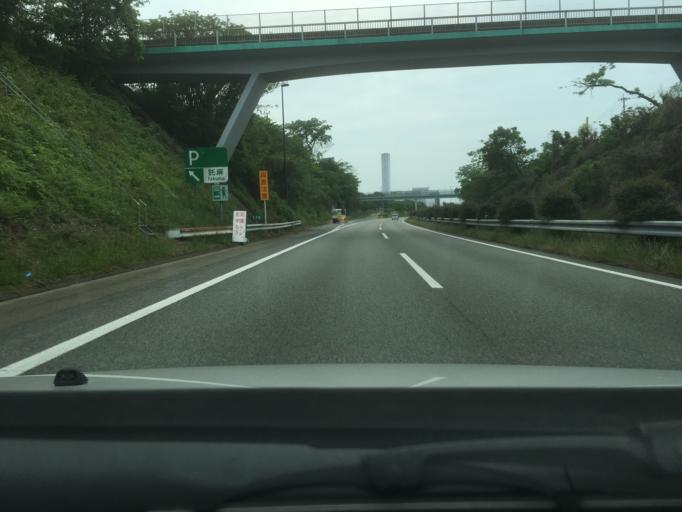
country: JP
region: Kumamoto
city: Ozu
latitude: 32.8130
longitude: 130.7930
